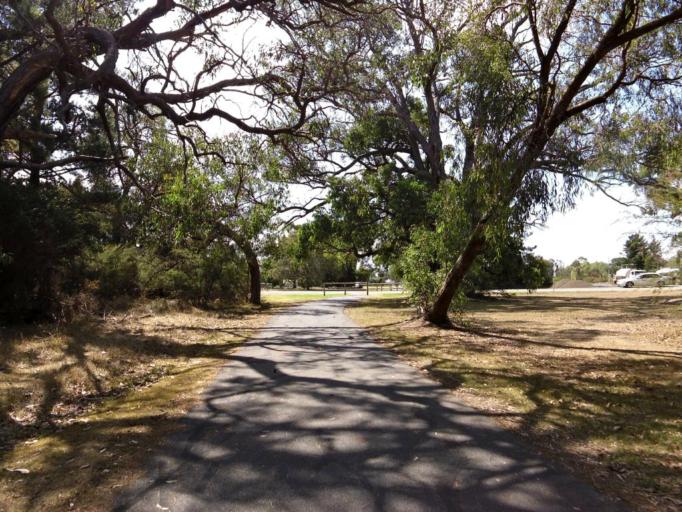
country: AU
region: Victoria
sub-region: Mornington Peninsula
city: Crib Point
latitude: -38.3402
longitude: 145.1755
